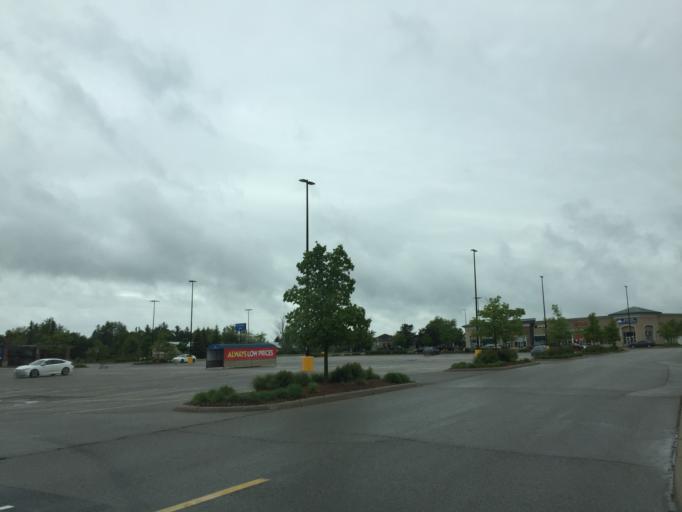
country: CA
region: Ontario
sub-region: Wellington County
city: Guelph
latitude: 43.5649
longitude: -80.2793
